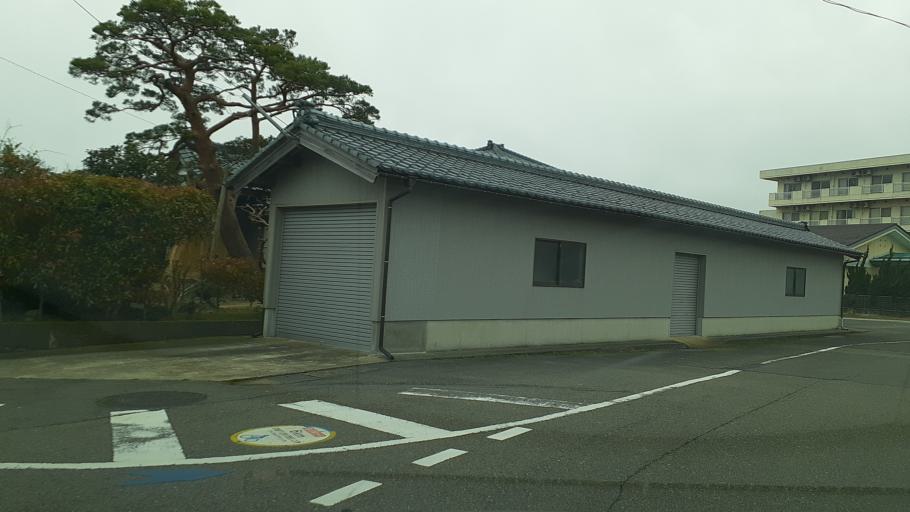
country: JP
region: Niigata
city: Niigata-shi
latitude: 37.8733
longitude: 139.0617
